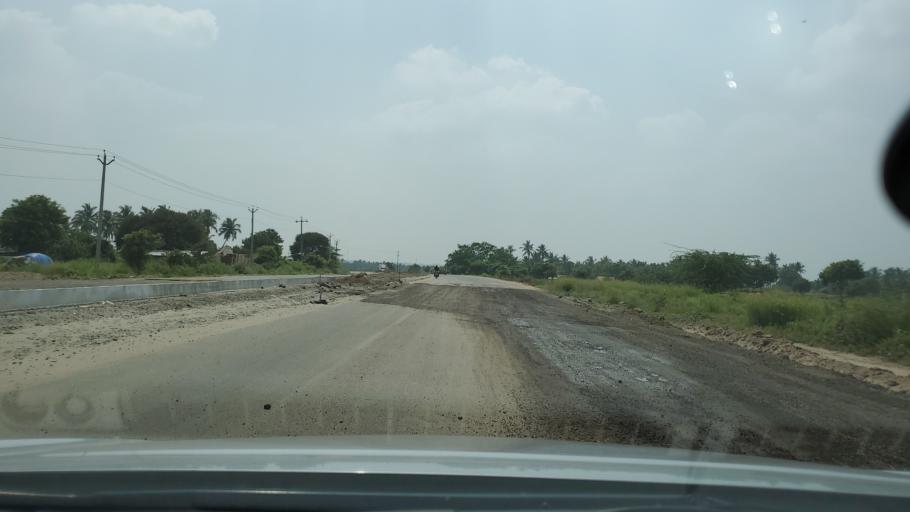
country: IN
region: Tamil Nadu
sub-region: Tiruppur
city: Kangayam
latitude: 10.9312
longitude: 77.4430
